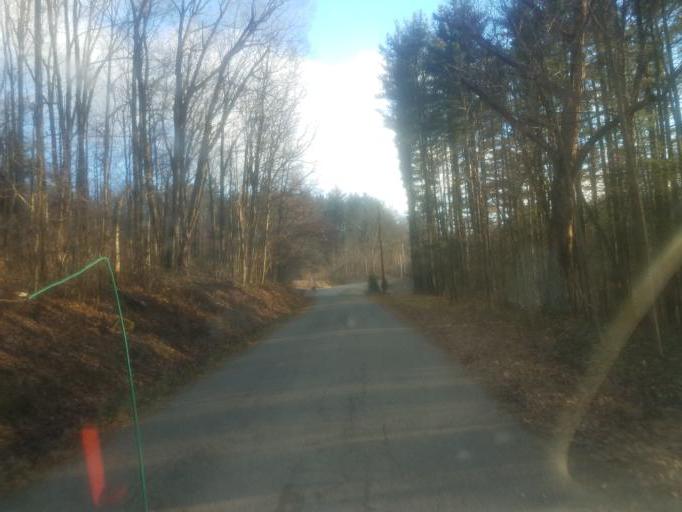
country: US
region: Ohio
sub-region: Sandusky County
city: Bellville
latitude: 40.5945
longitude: -82.3914
